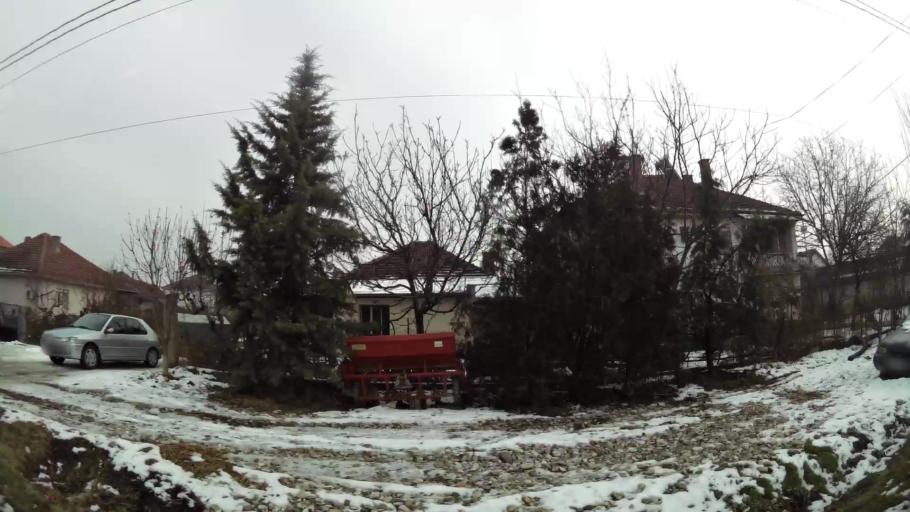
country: MK
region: Ilinden
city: Ilinden
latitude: 41.9937
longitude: 21.5736
